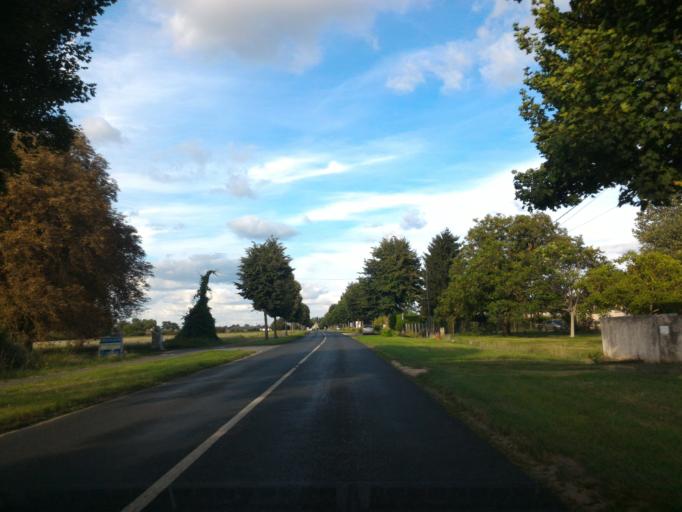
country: FR
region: Centre
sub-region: Departement du Loir-et-Cher
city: Muides-sur-Loire
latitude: 47.6634
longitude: 1.5166
